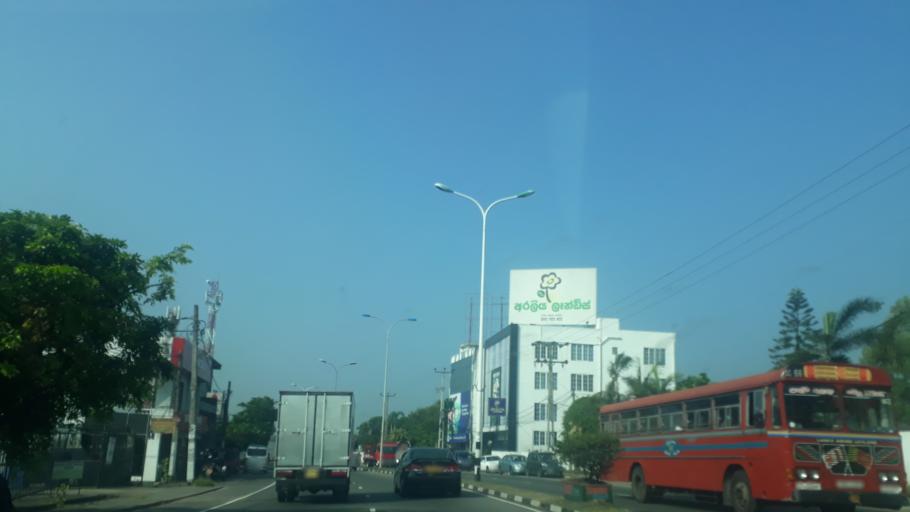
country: LK
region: Western
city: Kelaniya
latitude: 6.9940
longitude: 79.9445
